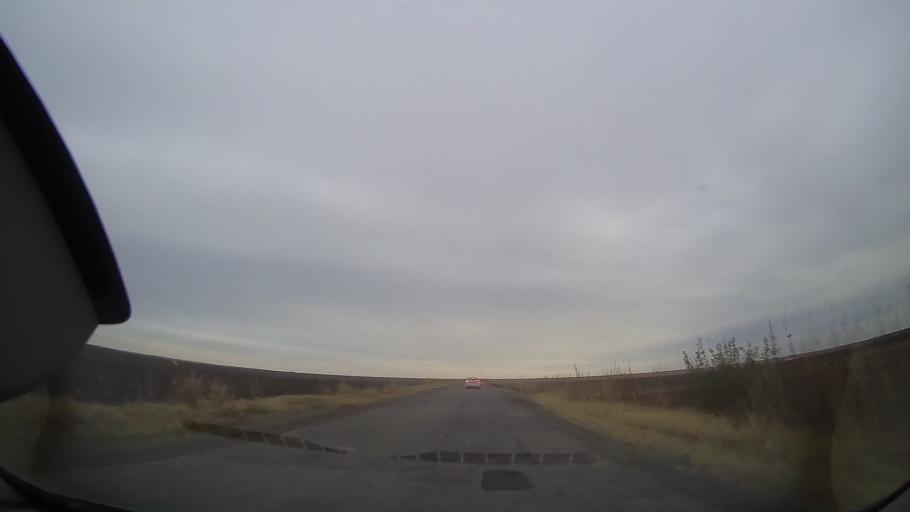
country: RO
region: Ialomita
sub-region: Oras Amara
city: Amara
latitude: 44.6644
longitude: 27.3007
